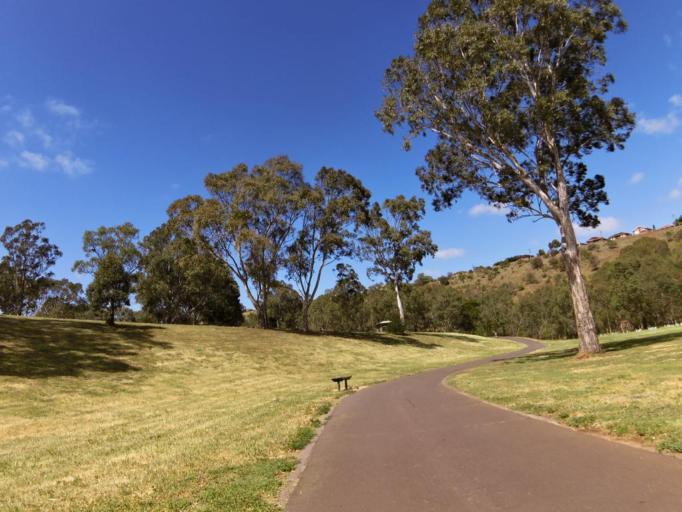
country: AU
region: Victoria
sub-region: Brimbank
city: Kealba
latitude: -37.7324
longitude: 144.8300
